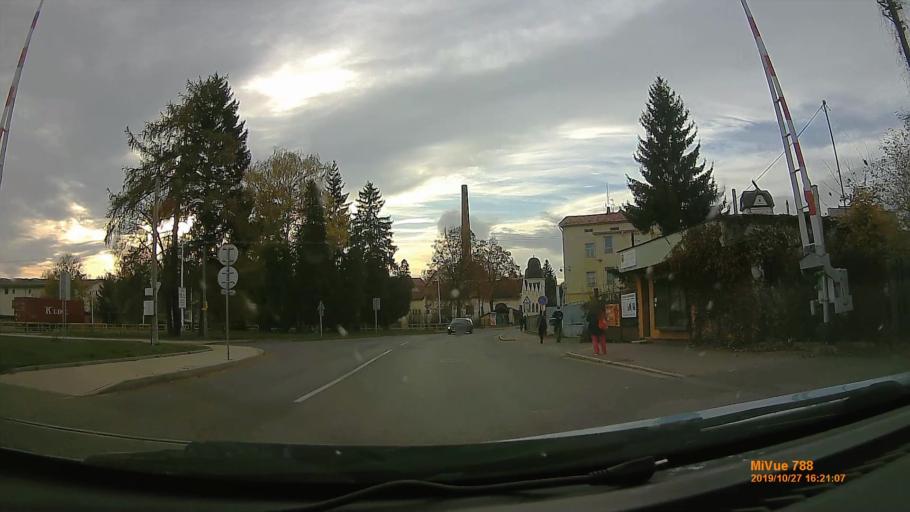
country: CZ
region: Kralovehradecky
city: Broumov
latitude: 50.5821
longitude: 16.3391
